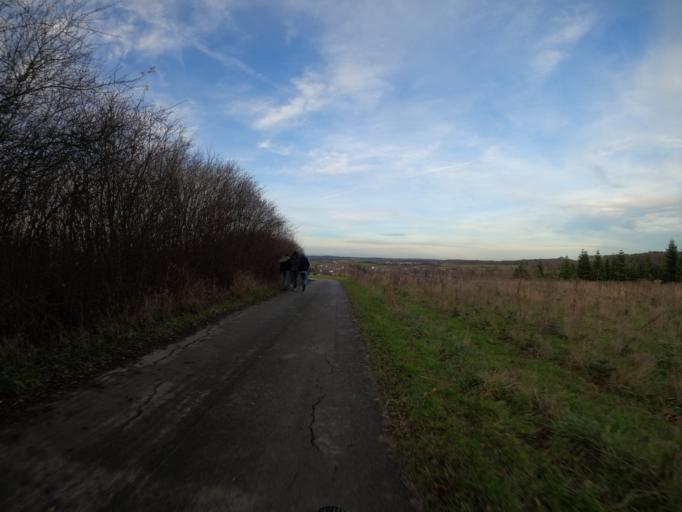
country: DE
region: Baden-Wuerttemberg
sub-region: Regierungsbezirk Stuttgart
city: Hattenhofen
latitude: 48.6582
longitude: 9.5743
